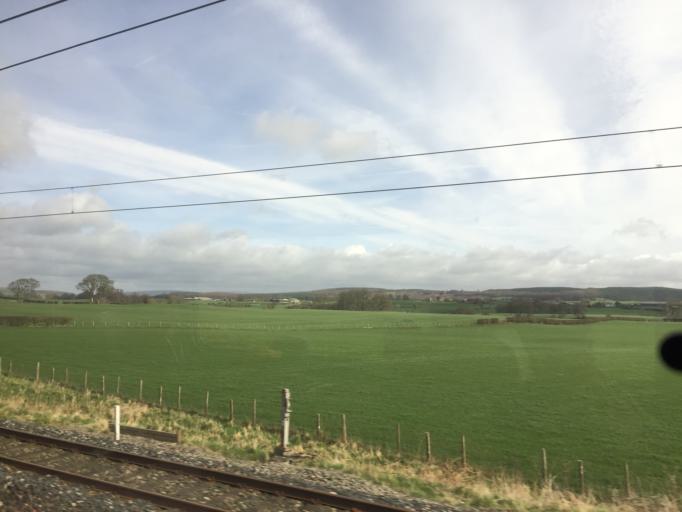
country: GB
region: England
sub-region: Cumbria
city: Penrith
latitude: 54.7268
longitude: -2.7981
